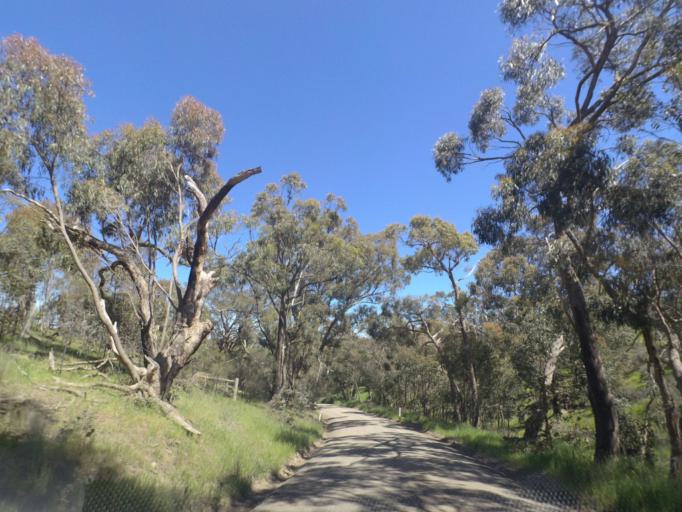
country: AU
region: Victoria
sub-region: Whittlesea
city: Whittlesea
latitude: -37.2832
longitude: 145.0074
